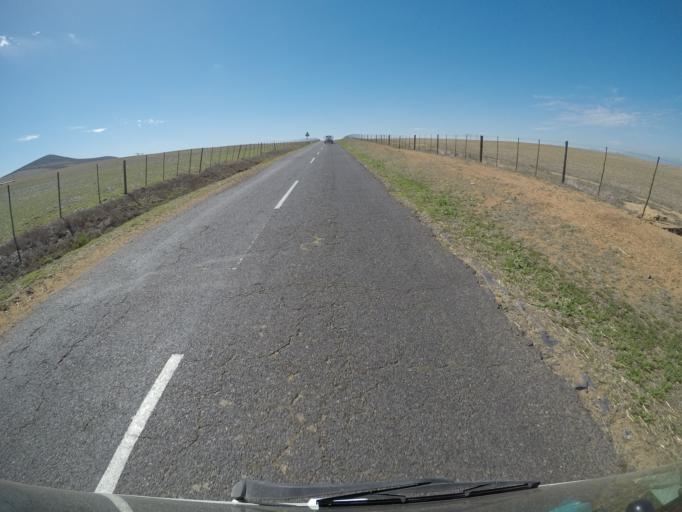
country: ZA
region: Western Cape
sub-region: City of Cape Town
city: Sunset Beach
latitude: -33.7400
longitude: 18.5641
